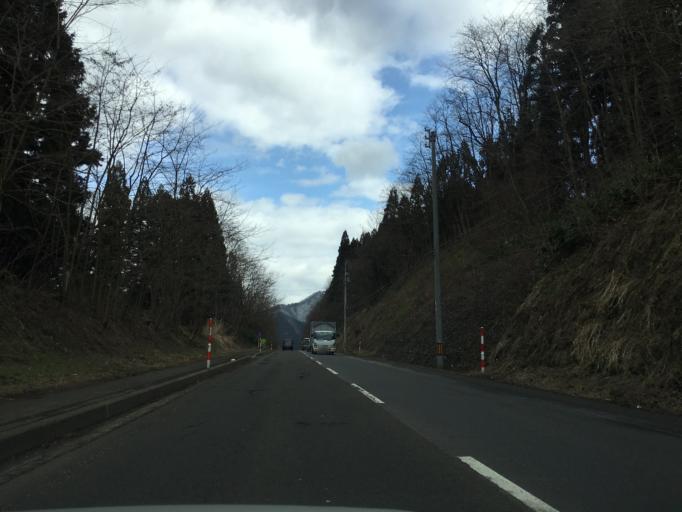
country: JP
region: Akita
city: Odate
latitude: 40.2222
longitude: 140.6574
